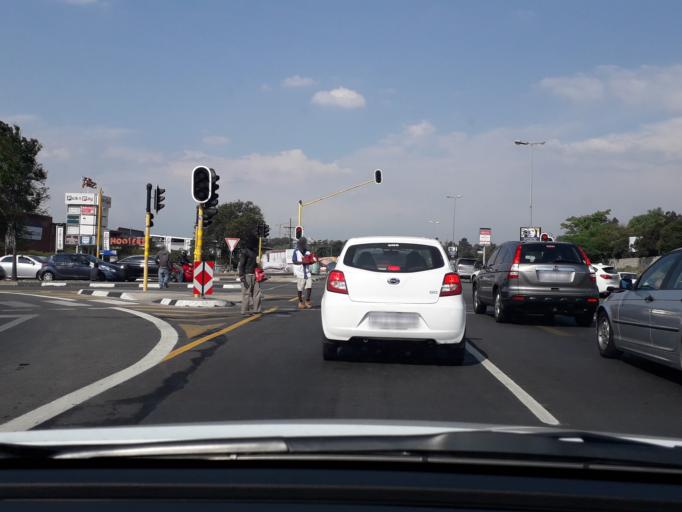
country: ZA
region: Gauteng
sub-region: City of Johannesburg Metropolitan Municipality
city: Diepsloot
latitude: -26.0253
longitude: 27.9902
